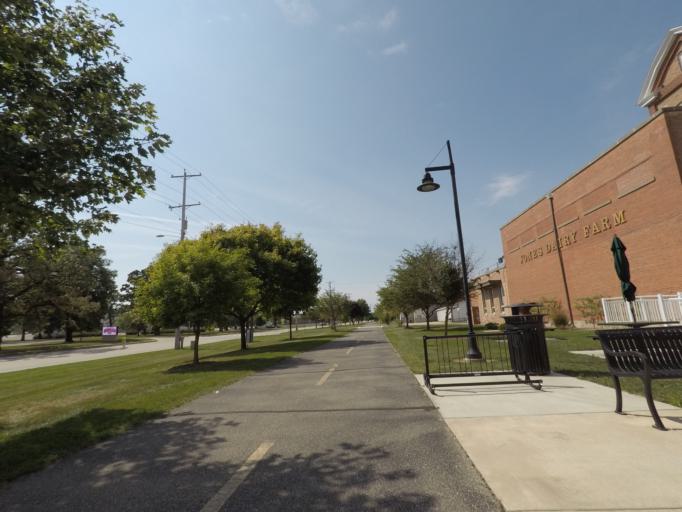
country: US
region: Wisconsin
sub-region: Jefferson County
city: Fort Atkinson
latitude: 42.9215
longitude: -88.8446
